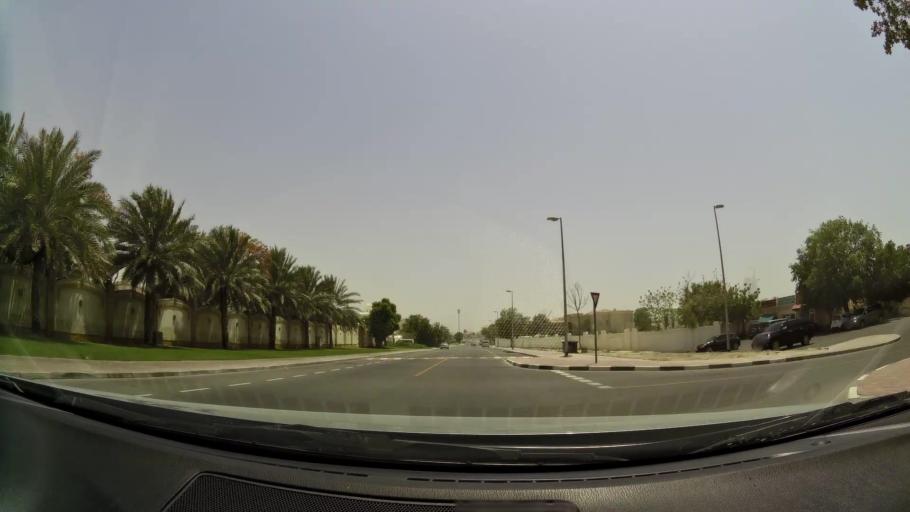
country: AE
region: Dubai
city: Dubai
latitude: 25.1478
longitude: 55.2064
